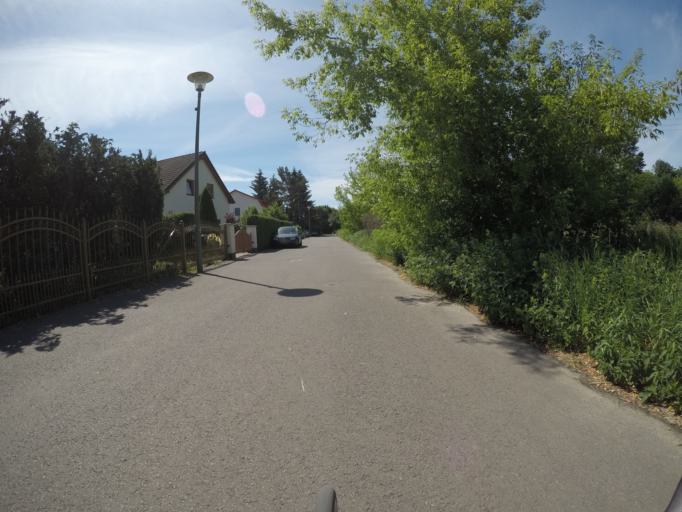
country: DE
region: Berlin
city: Biesdorf
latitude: 52.5067
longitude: 13.5422
